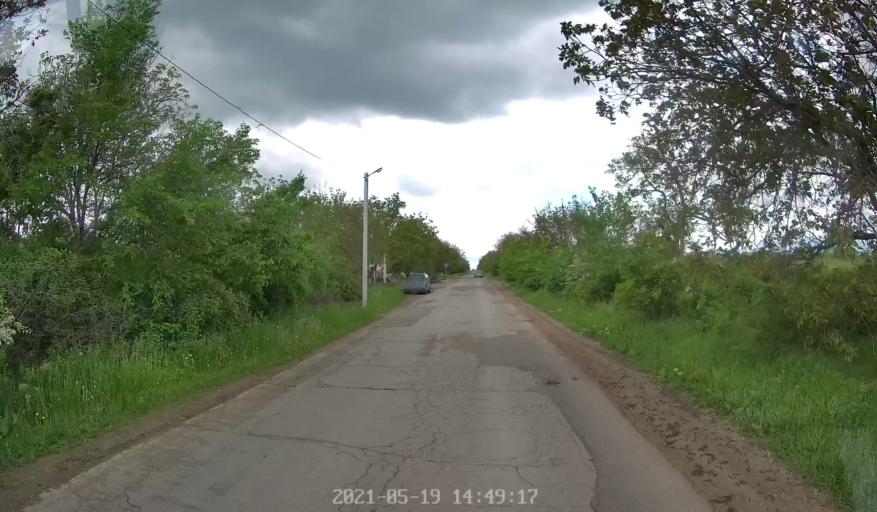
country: MD
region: Chisinau
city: Stauceni
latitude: 47.0487
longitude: 28.9528
